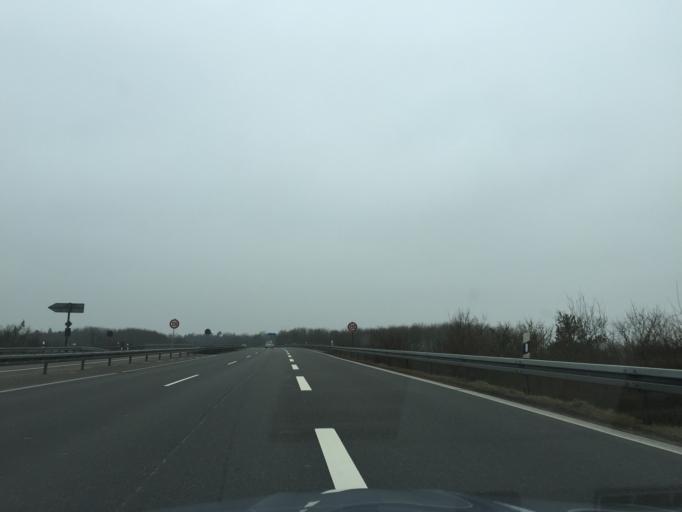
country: DE
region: Baden-Wuerttemberg
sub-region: Karlsruhe Region
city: Ketsch
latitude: 49.3595
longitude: 8.5490
